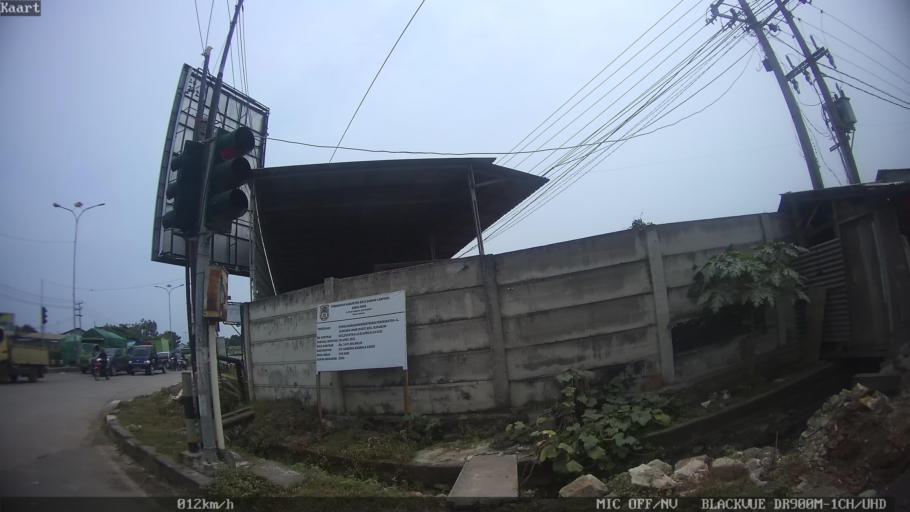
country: ID
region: Lampung
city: Bandarlampung
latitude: -5.4076
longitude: 105.2936
